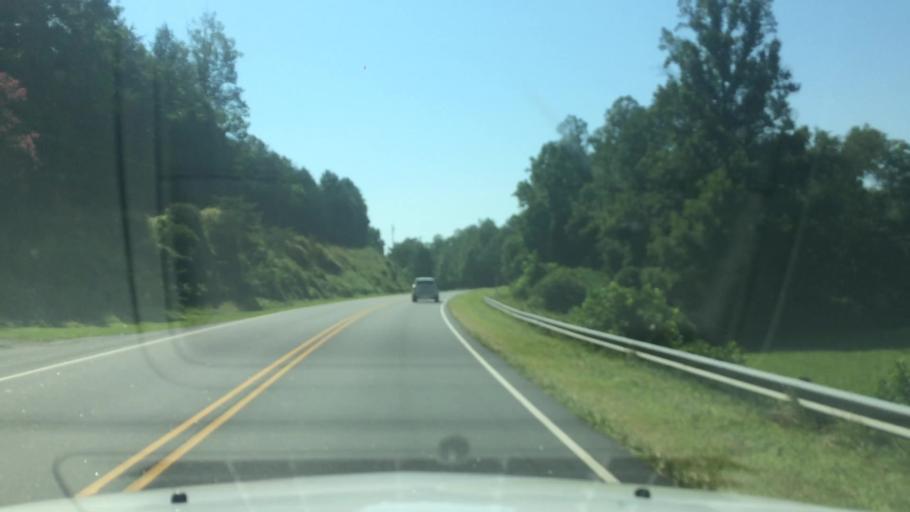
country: US
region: North Carolina
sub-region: Caldwell County
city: Hudson
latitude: 35.9174
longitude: -81.4552
